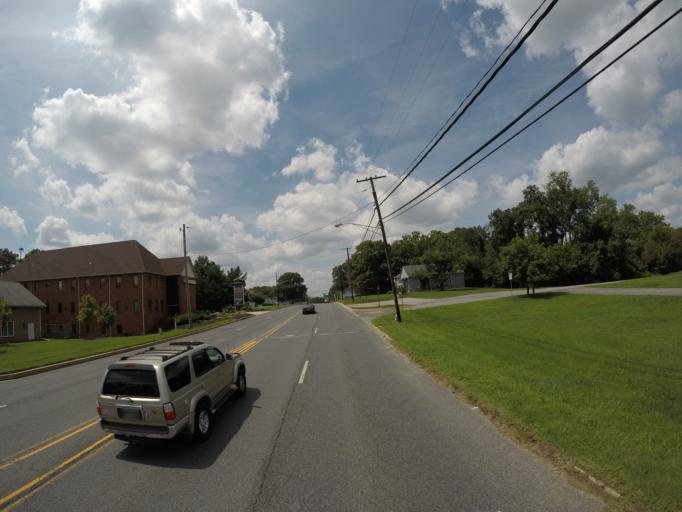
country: US
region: Maryland
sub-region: Anne Arundel County
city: Odenton
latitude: 39.0904
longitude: -76.7085
